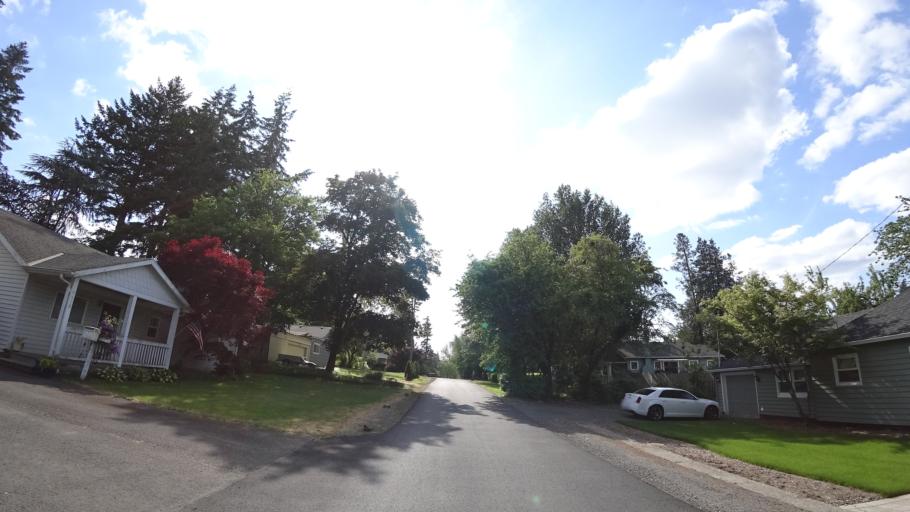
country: US
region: Oregon
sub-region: Washington County
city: Garden Home-Whitford
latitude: 45.4641
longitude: -122.7234
